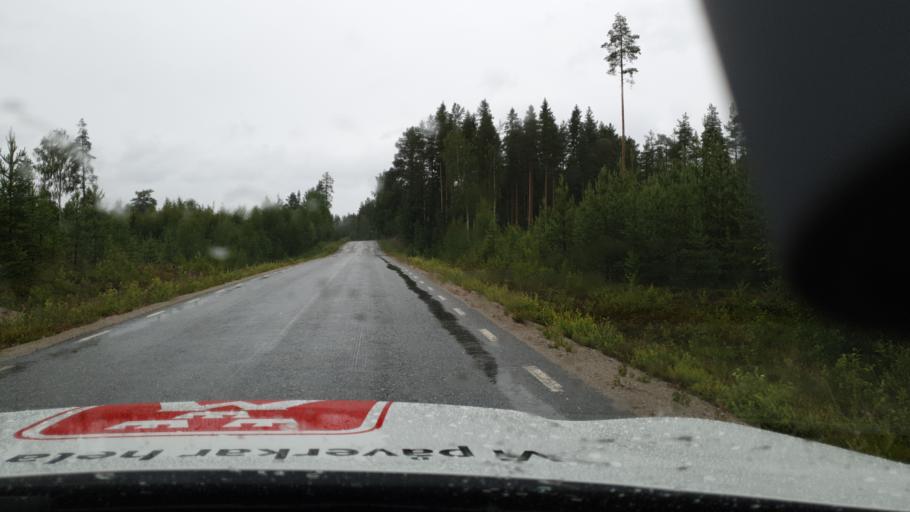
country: SE
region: Vaesterbotten
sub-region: Vindelns Kommun
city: Vindeln
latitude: 64.4968
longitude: 19.8015
